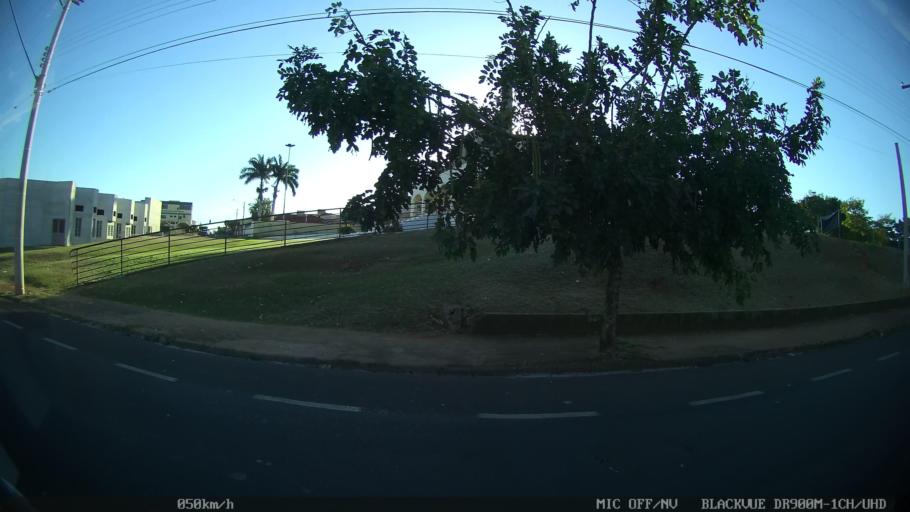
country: BR
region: Sao Paulo
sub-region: Sao Jose Do Rio Preto
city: Sao Jose do Rio Preto
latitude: -20.8050
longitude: -49.3607
